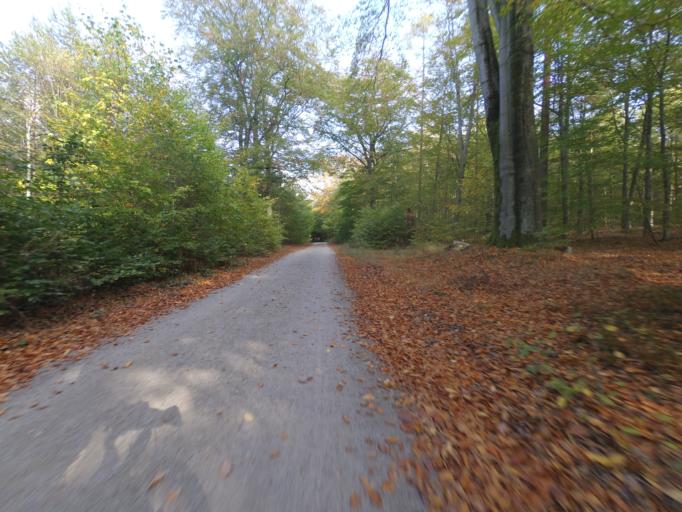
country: DE
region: Saxony
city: Albertstadt
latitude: 51.0991
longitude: 13.8060
